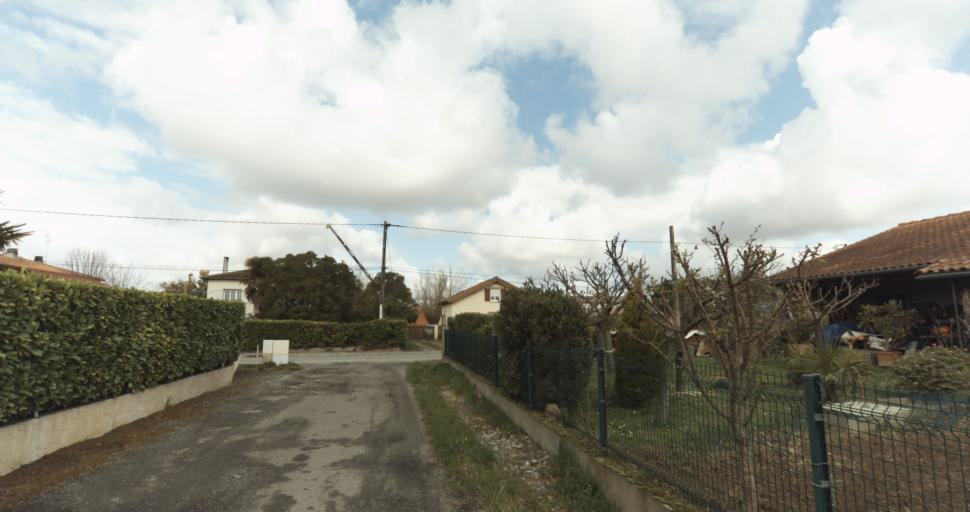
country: FR
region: Midi-Pyrenees
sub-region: Departement de la Haute-Garonne
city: Auterive
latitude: 43.3469
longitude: 1.4626
